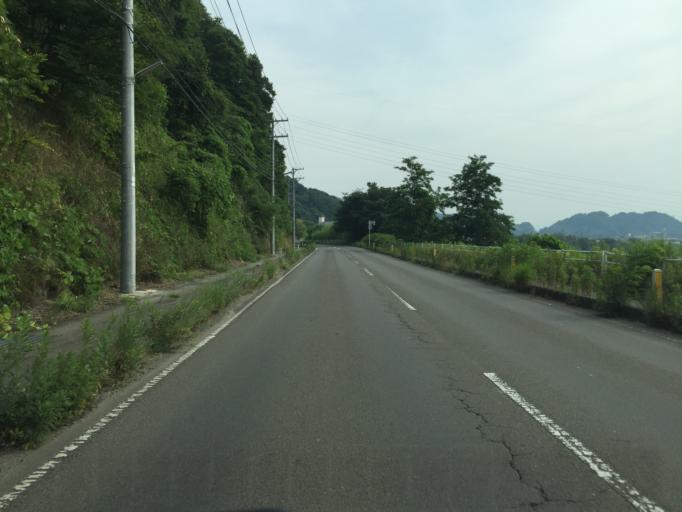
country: JP
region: Fukushima
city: Fukushima-shi
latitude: 37.7561
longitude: 140.4876
